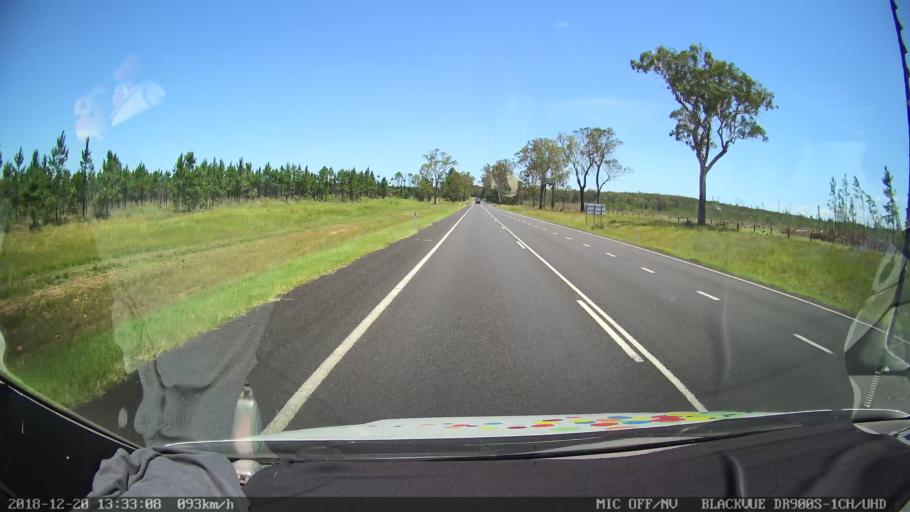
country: AU
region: New South Wales
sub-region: Clarence Valley
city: Gordon
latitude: -29.2413
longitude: 152.9876
